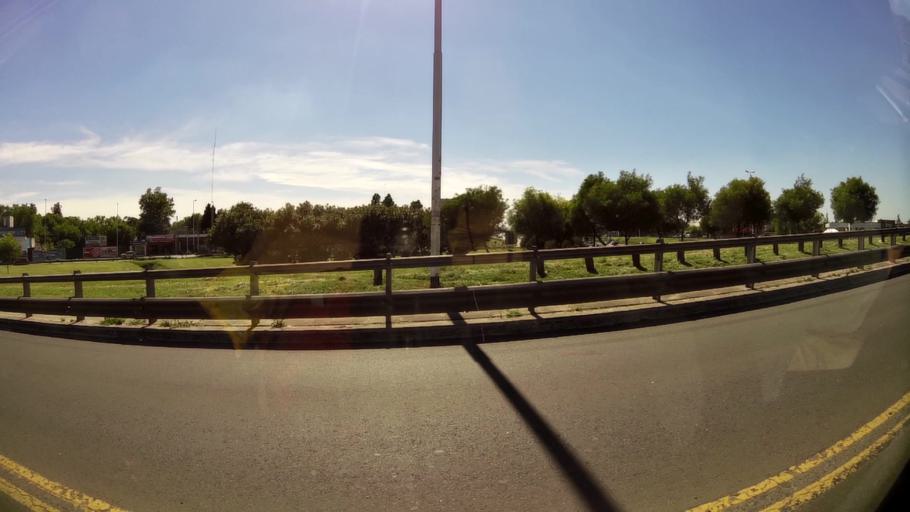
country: AR
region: Buenos Aires
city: Ituzaingo
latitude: -34.6310
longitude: -58.6536
